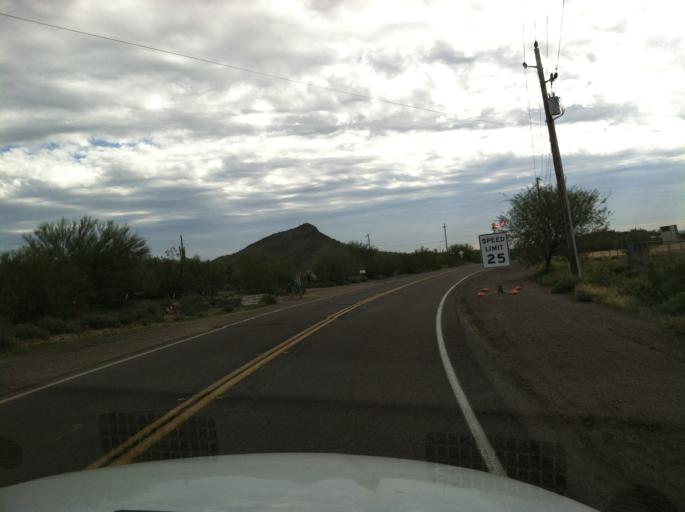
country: US
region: Arizona
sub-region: Maricopa County
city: New River
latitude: 33.9006
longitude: -112.0780
